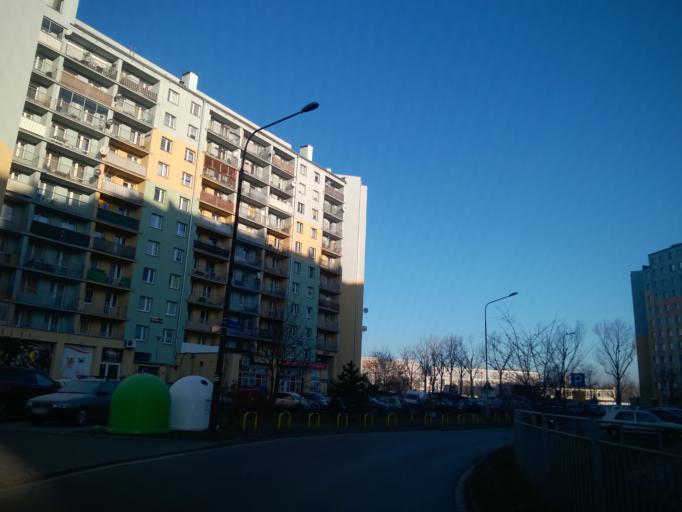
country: PL
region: Lower Silesian Voivodeship
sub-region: Powiat wroclawski
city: Wroclaw
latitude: 51.0801
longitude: 17.0405
